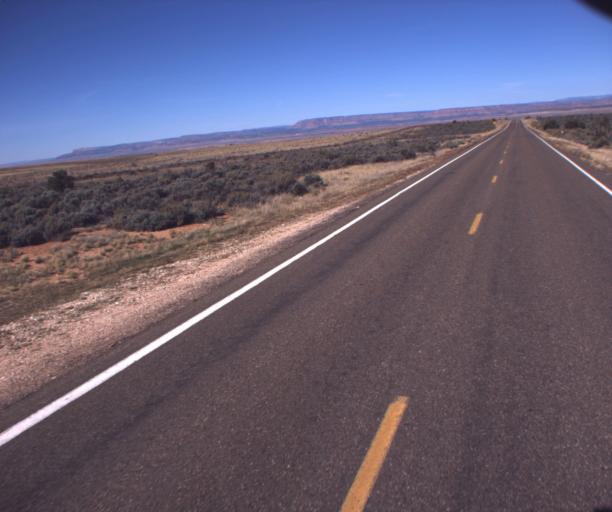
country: US
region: Arizona
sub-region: Coconino County
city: Fredonia
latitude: 36.8682
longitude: -112.3214
